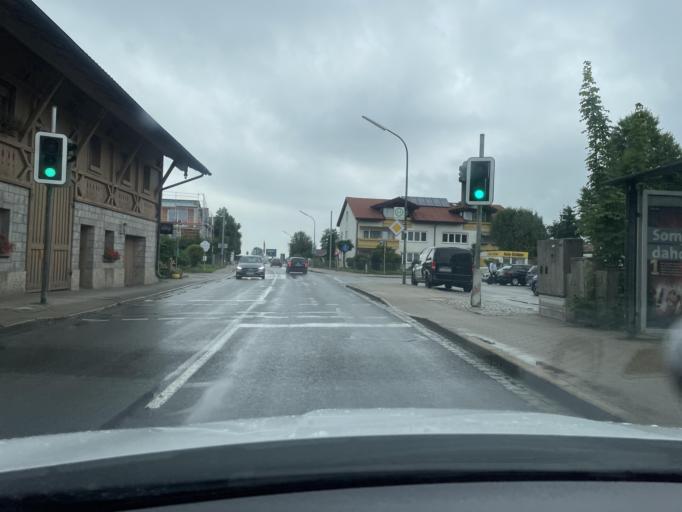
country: DE
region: Bavaria
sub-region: Upper Bavaria
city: Rosenheim
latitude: 47.8775
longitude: 12.1125
